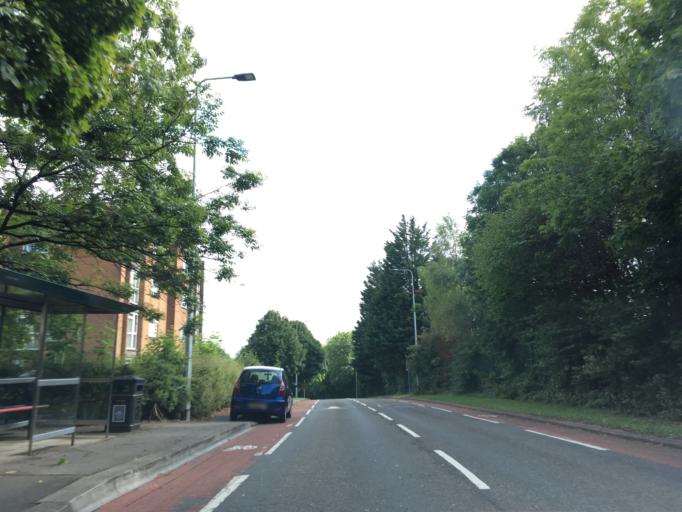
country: GB
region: Wales
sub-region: Cardiff
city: Cardiff
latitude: 51.5097
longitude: -3.1586
